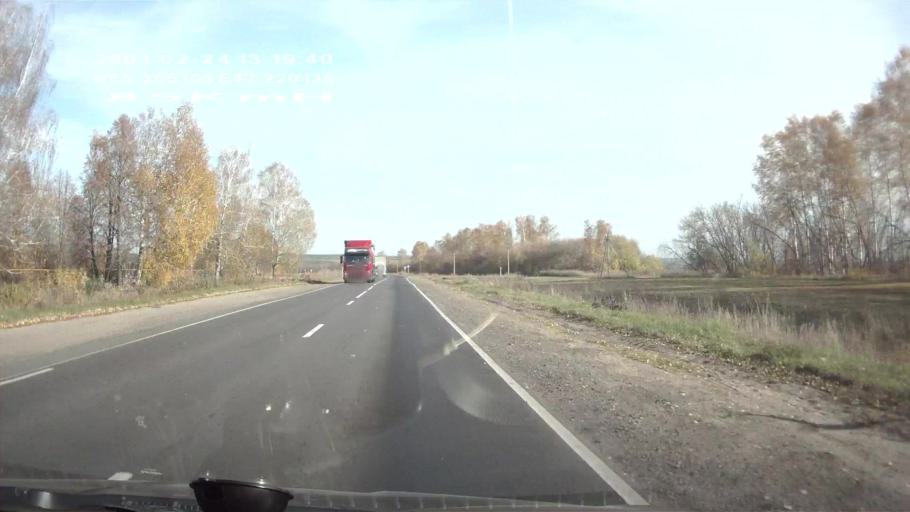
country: RU
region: Chuvashia
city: Ibresi
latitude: 55.3551
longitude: 47.2206
